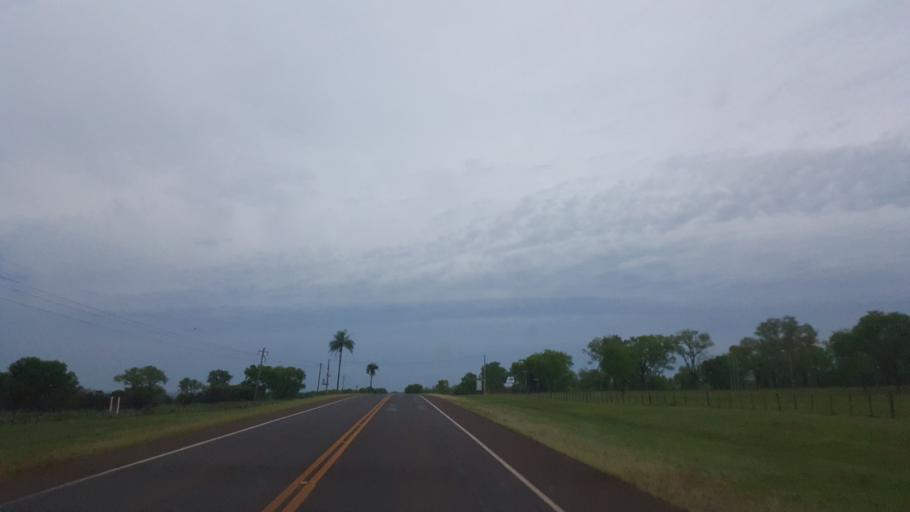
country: AR
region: Misiones
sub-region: Departamento de Apostoles
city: San Jose
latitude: -27.7247
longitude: -55.7904
